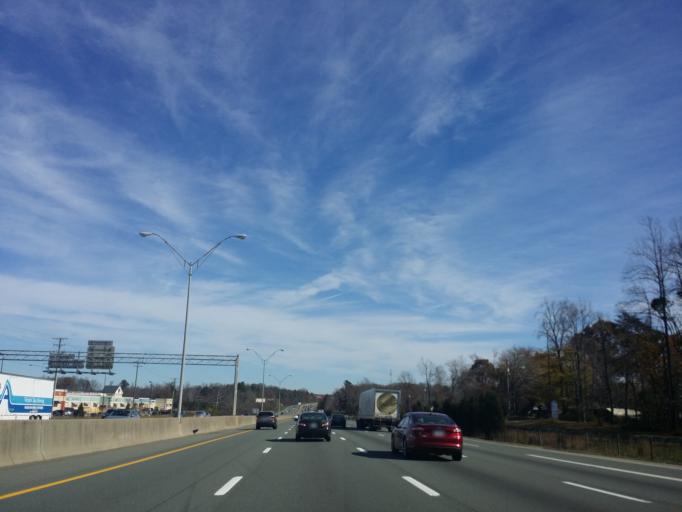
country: US
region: North Carolina
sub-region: Alamance County
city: Mebane
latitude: 36.0721
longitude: -79.2687
